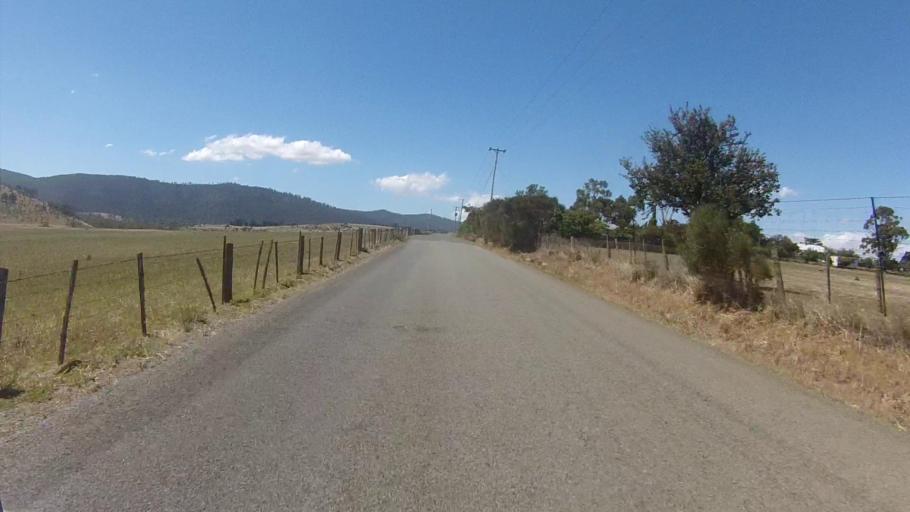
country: AU
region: Tasmania
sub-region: Sorell
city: Sorell
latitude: -42.7678
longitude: 147.5998
